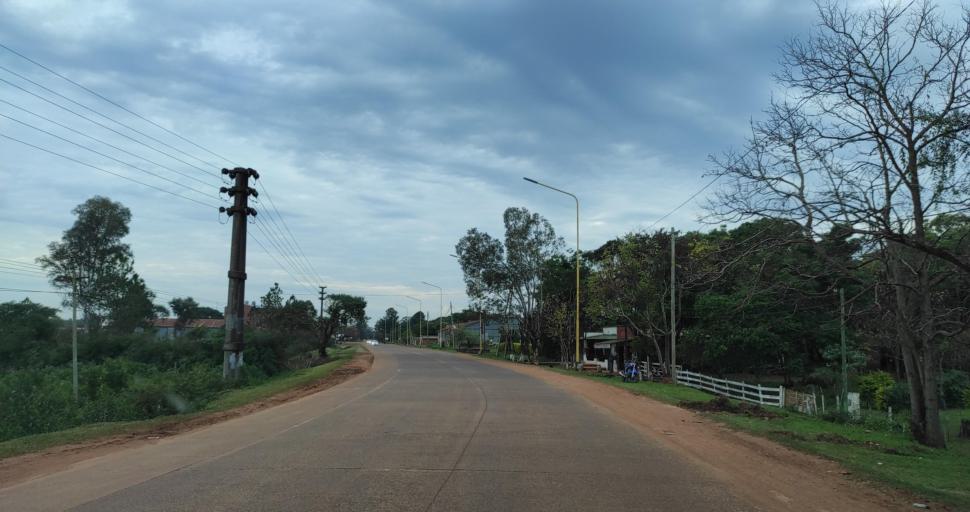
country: AR
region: Corrientes
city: Santo Tome
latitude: -28.5511
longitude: -56.0704
